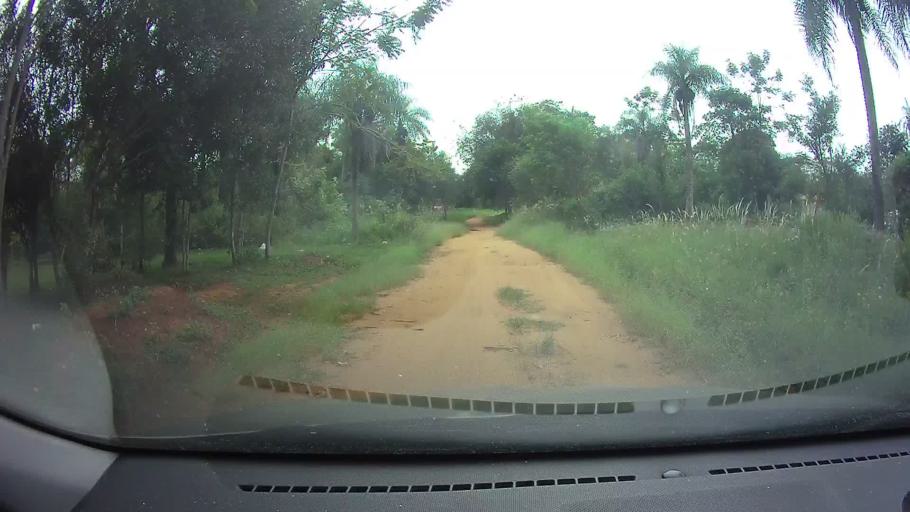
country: PY
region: Central
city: Limpio
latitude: -25.2381
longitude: -57.4596
